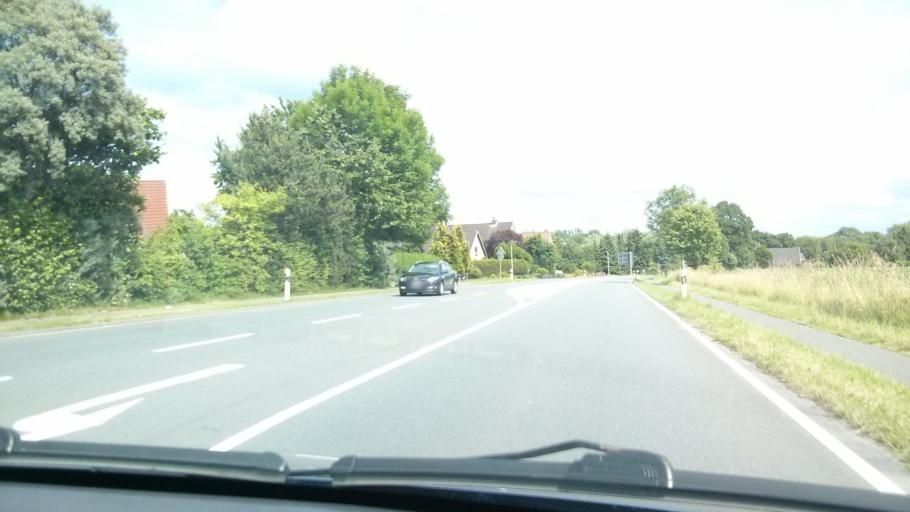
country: DE
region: Lower Saxony
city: Schiffdorf
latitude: 53.5263
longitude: 8.6586
